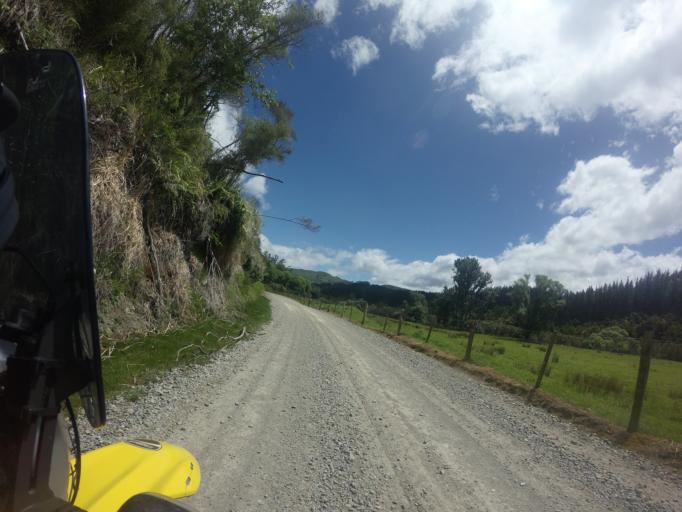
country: NZ
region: Hawke's Bay
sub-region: Wairoa District
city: Wairoa
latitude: -38.9879
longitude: 177.7581
